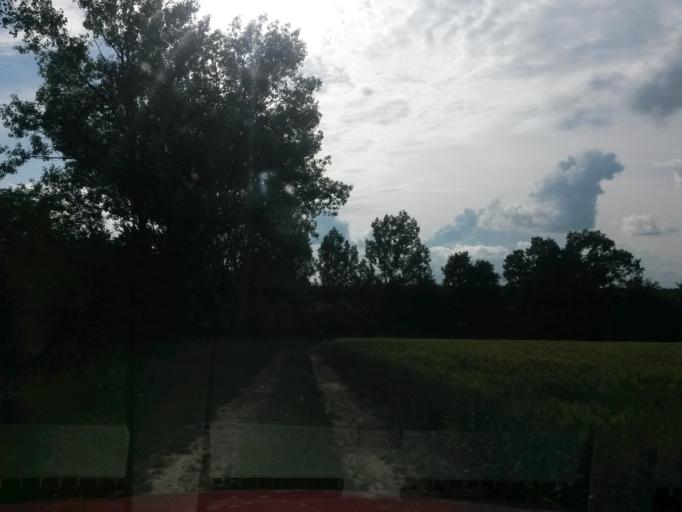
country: SK
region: Kosicky
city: Moldava nad Bodvou
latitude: 48.6214
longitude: 21.1035
